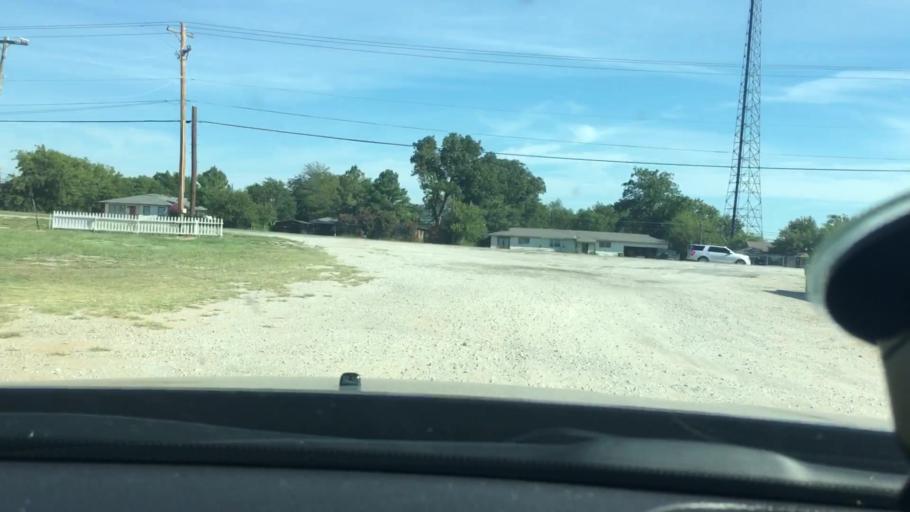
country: US
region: Oklahoma
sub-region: Carter County
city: Lone Grove
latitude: 34.1720
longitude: -97.2488
